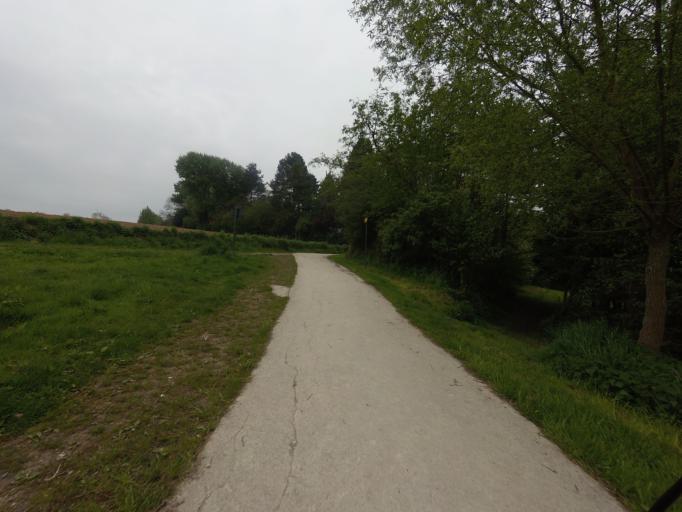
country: BE
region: Flanders
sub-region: Provincie Vlaams-Brabant
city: Grimbergen
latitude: 50.9207
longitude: 4.3980
